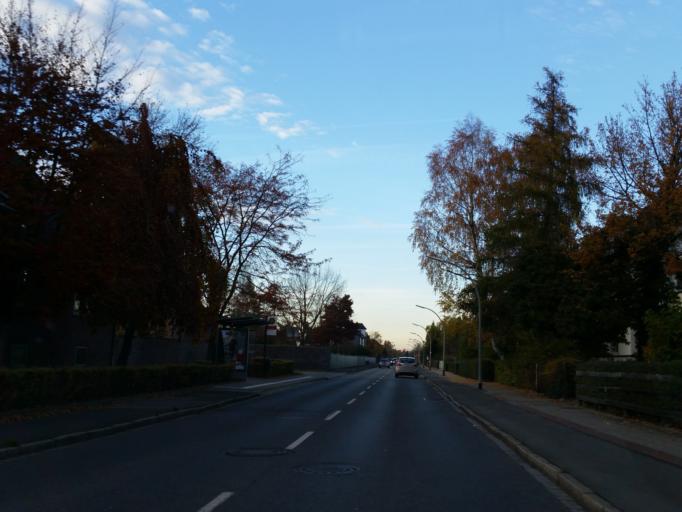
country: DE
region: Lower Saxony
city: Braunschweig
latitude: 52.2759
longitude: 10.5696
